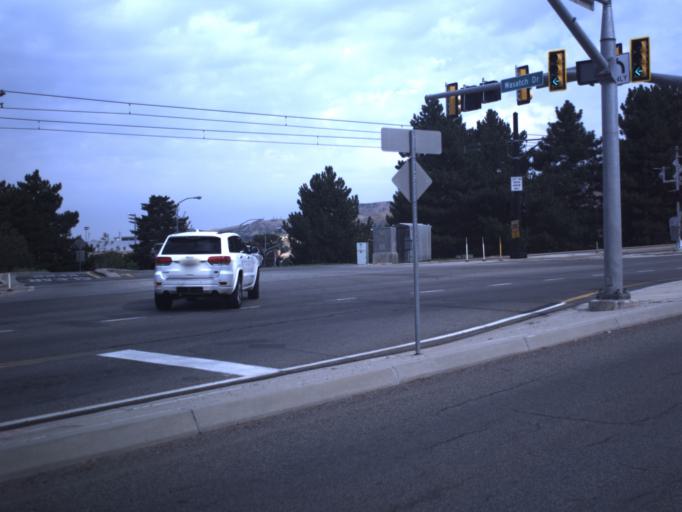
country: US
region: Utah
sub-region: Salt Lake County
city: Salt Lake City
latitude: 40.7656
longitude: -111.8368
